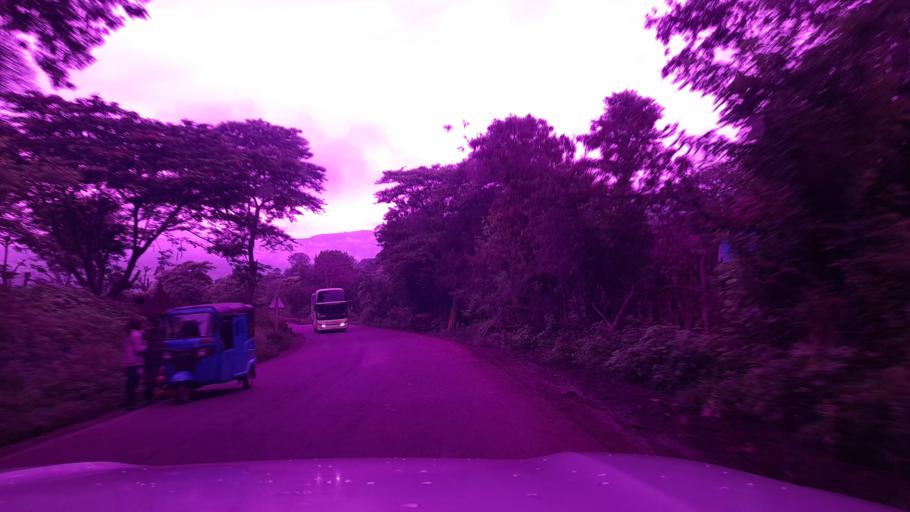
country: ET
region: Oromiya
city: Waliso
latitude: 8.2247
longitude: 37.5746
